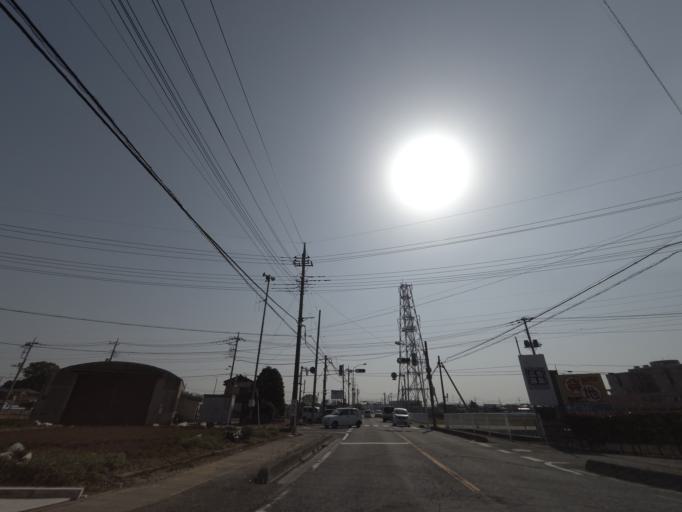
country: JP
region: Saitama
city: Yono
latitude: 35.8841
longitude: 139.5964
